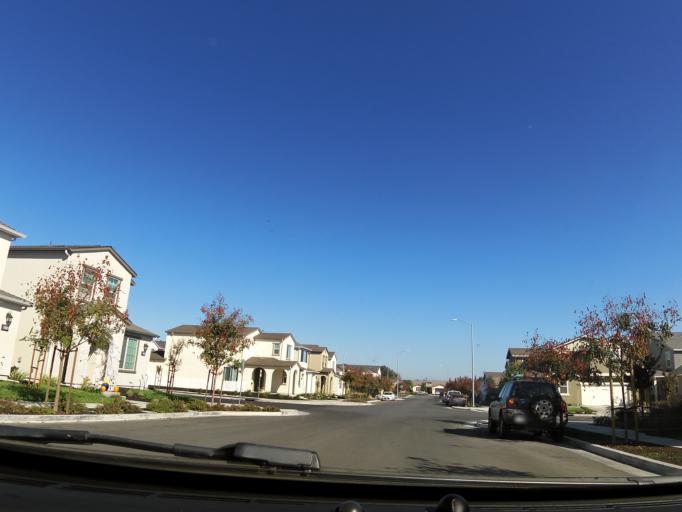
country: US
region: California
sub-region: San Benito County
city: Hollister
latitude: 36.8306
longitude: -121.3991
